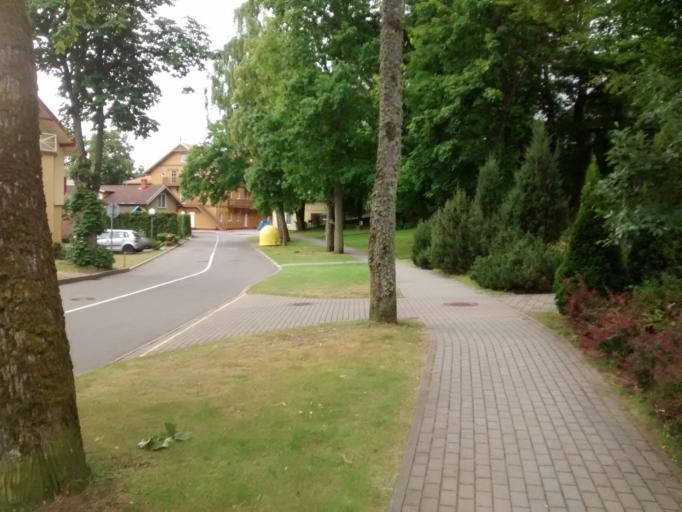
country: LT
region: Klaipedos apskritis
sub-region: Klaipeda
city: Klaipeda
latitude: 55.5423
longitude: 21.1202
